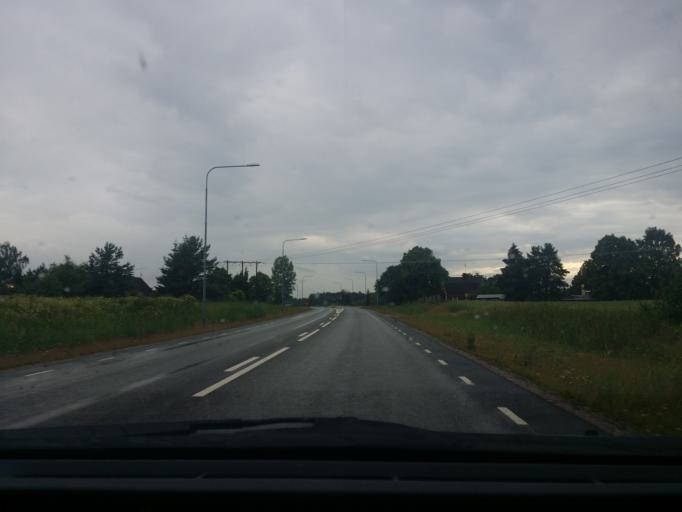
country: SE
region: Vaestmanland
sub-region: Arboga Kommun
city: Arboga
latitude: 59.4040
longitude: 15.8569
